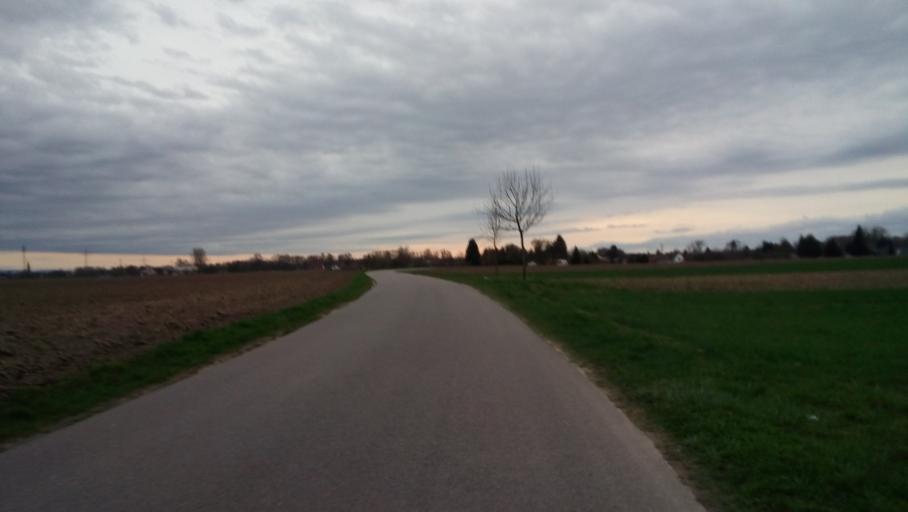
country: DE
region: Baden-Wuerttemberg
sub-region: Karlsruhe Region
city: Lichtenau
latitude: 48.7118
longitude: 7.9789
